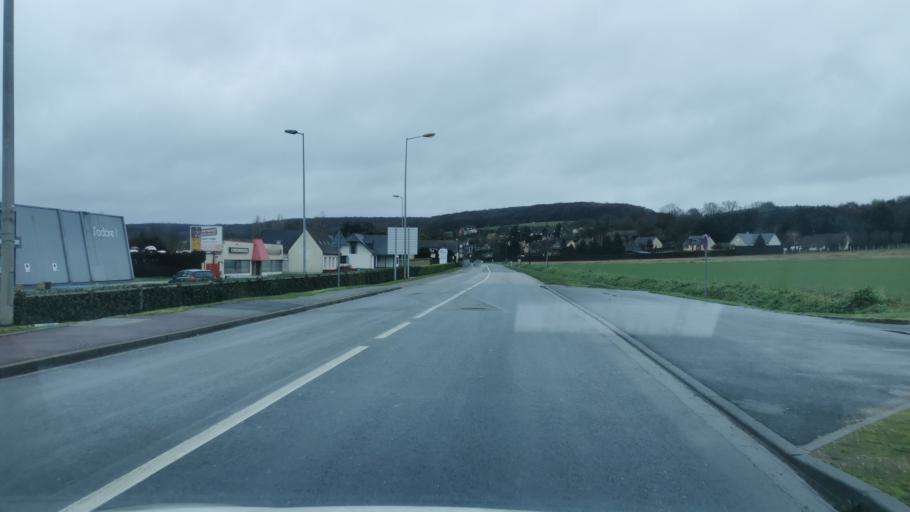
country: FR
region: Haute-Normandie
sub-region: Departement de l'Eure
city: Gravigny
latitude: 49.0617
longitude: 1.1711
